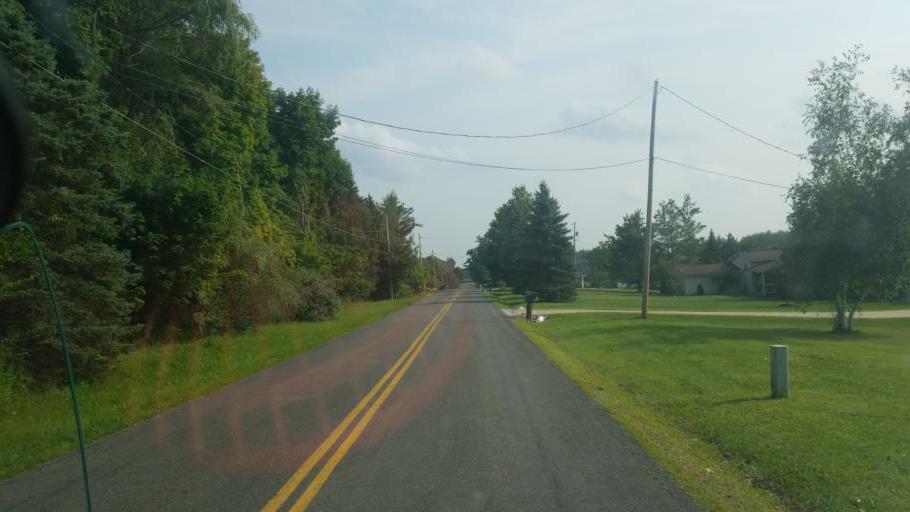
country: US
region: Ohio
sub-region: Medina County
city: Seville
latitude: 41.0737
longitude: -81.8849
